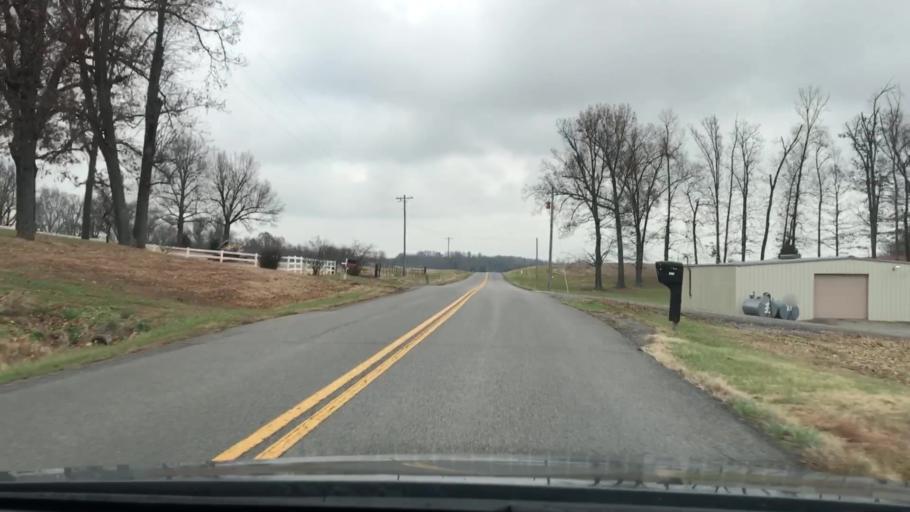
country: US
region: Kentucky
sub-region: Webster County
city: Sebree
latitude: 37.4905
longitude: -87.4624
